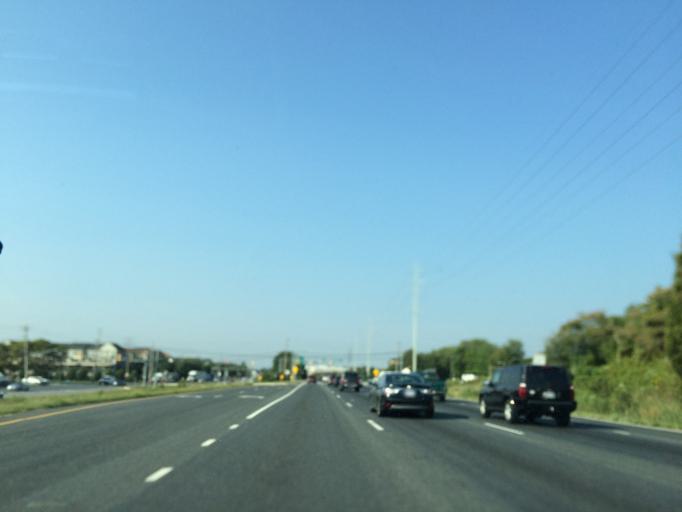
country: US
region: Maryland
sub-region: Anne Arundel County
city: Gambrills
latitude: 39.0403
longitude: -76.6736
